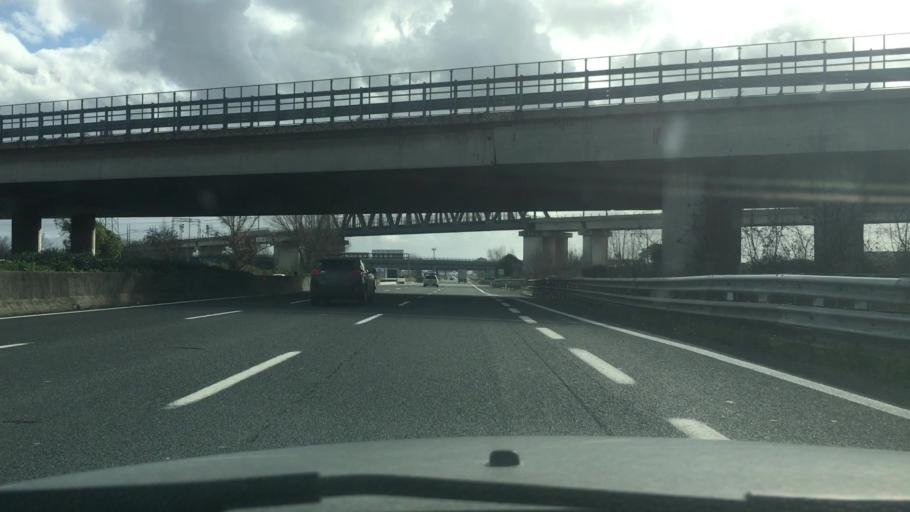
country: IT
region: Campania
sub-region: Provincia di Caserta
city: San Marco Evangelista
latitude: 41.0155
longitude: 14.3224
